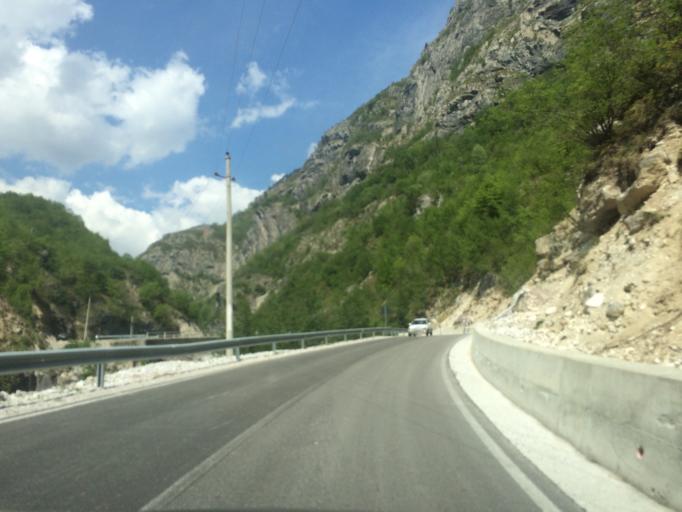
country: AL
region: Kukes
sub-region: Rrethi i Tropojes
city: Bajram Curri
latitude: 42.4120
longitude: 20.0209
